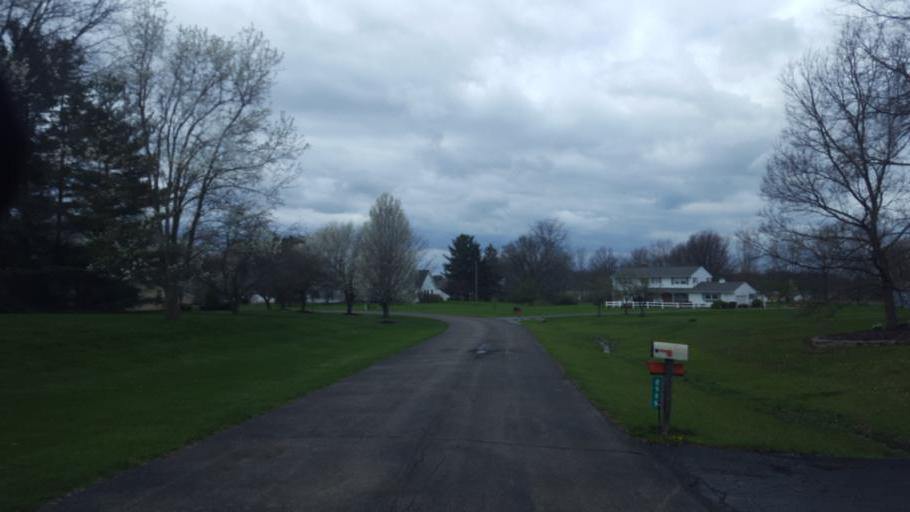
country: US
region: Ohio
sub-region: Franklin County
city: Westerville
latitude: 40.1426
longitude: -82.8703
